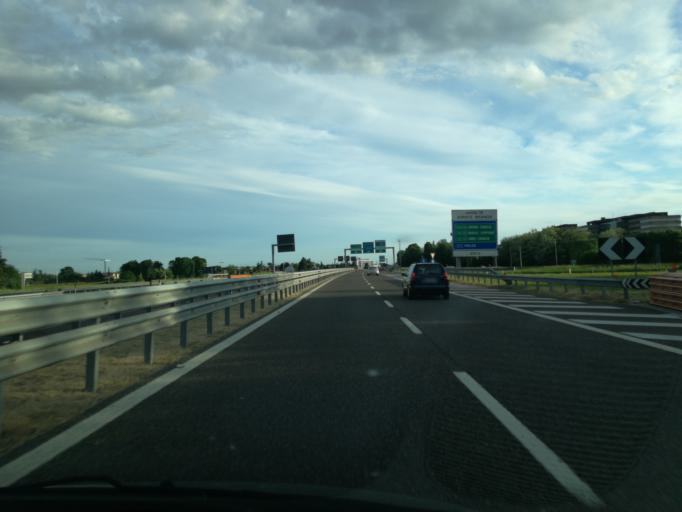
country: IT
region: Lombardy
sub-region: Provincia di Monza e Brianza
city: Agrate Brianza
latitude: 45.5770
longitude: 9.3420
